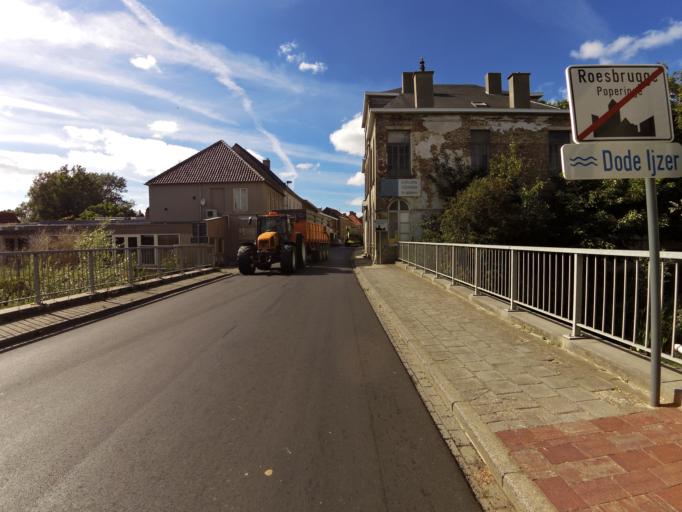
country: FR
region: Nord-Pas-de-Calais
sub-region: Departement du Nord
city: Hondschoote
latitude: 50.9212
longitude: 2.6210
